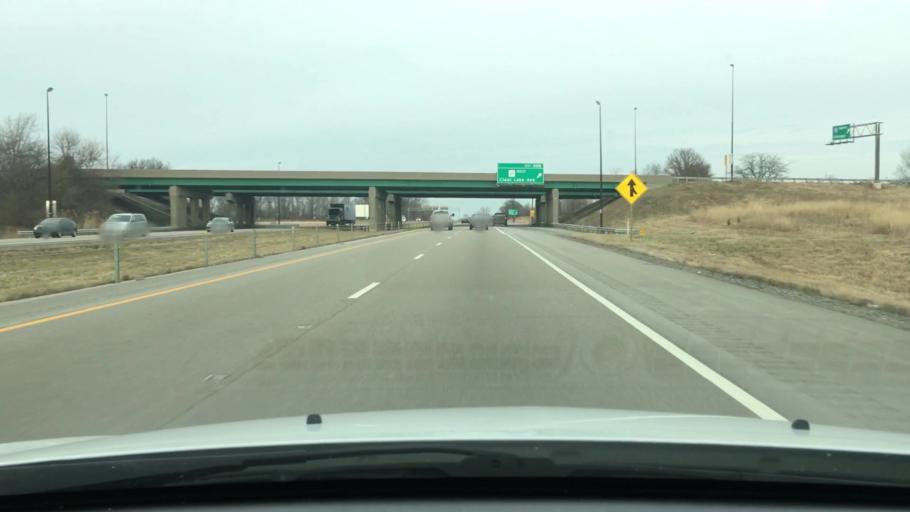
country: US
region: Illinois
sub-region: Sangamon County
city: Grandview
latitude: 39.8007
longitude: -89.5954
